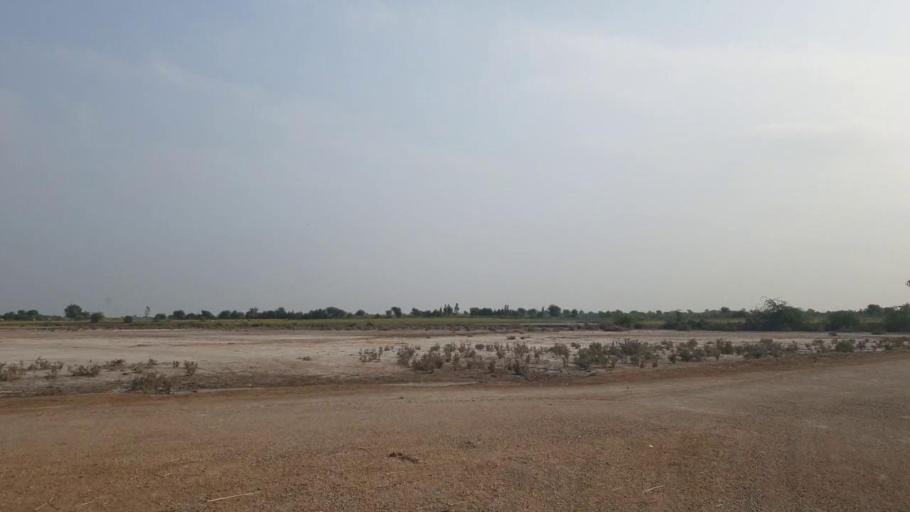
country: PK
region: Sindh
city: Badin
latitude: 24.5997
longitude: 68.7014
